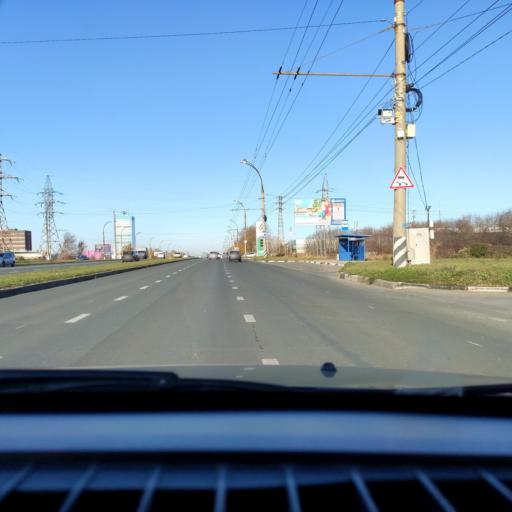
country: RU
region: Samara
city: Tol'yatti
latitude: 53.5455
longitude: 49.2655
